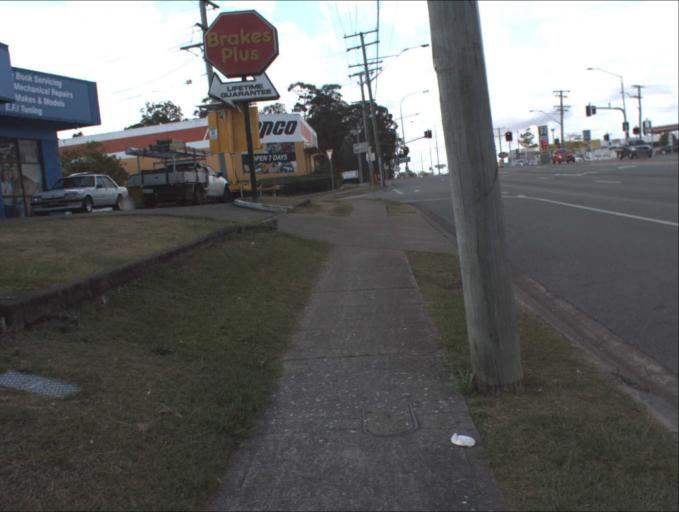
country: AU
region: Queensland
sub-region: Logan
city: Springwood
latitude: -27.6192
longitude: 153.1158
